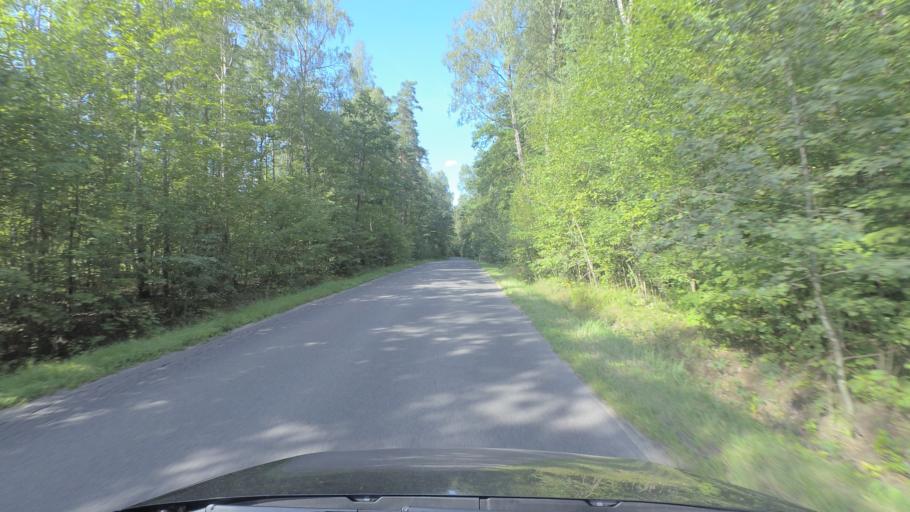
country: LT
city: Nemencine
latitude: 54.8153
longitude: 25.3517
